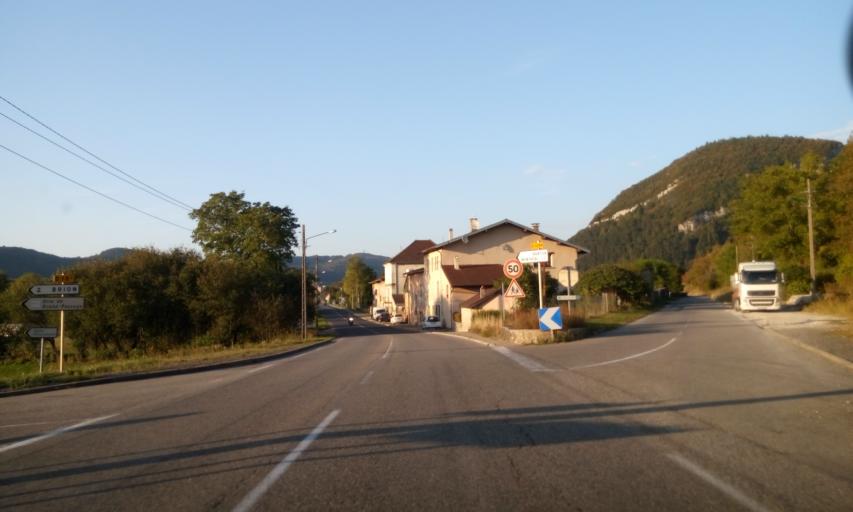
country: FR
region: Rhone-Alpes
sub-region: Departement de l'Ain
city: Montreal-la-Cluse
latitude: 46.1599
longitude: 5.5699
